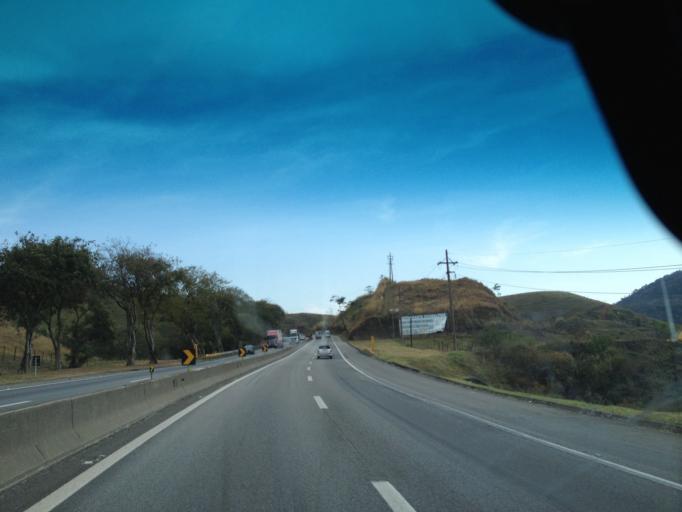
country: BR
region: Rio de Janeiro
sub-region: Porto Real
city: Porto Real
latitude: -22.4809
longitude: -44.2614
